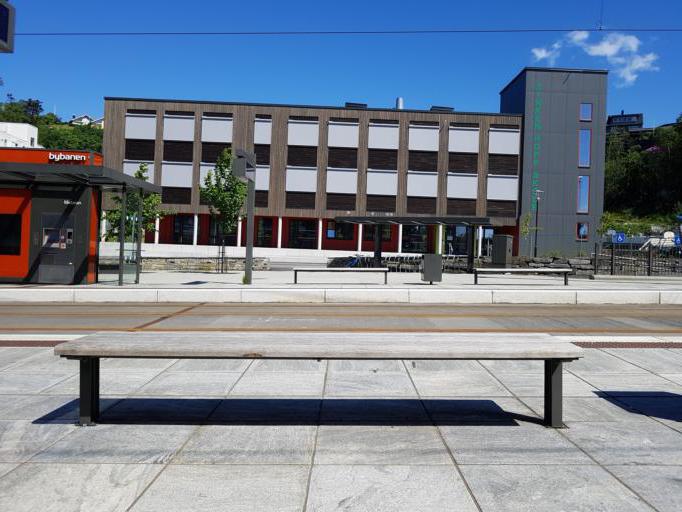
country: NO
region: Hordaland
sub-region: Bergen
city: Sandsli
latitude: 60.3010
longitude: 5.3089
